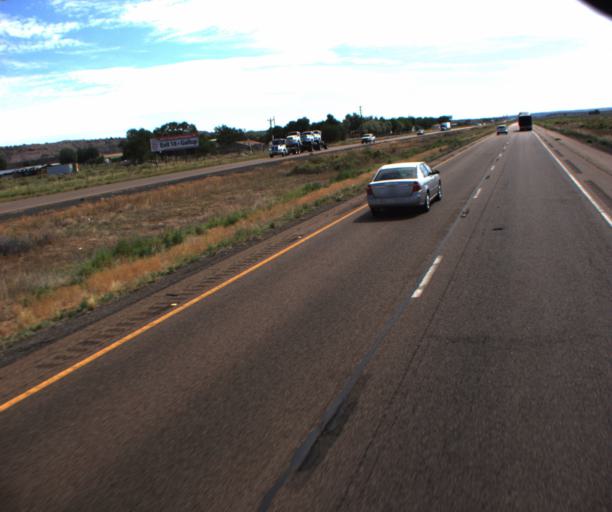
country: US
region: Arizona
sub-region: Apache County
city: Houck
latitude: 35.1990
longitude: -109.3947
